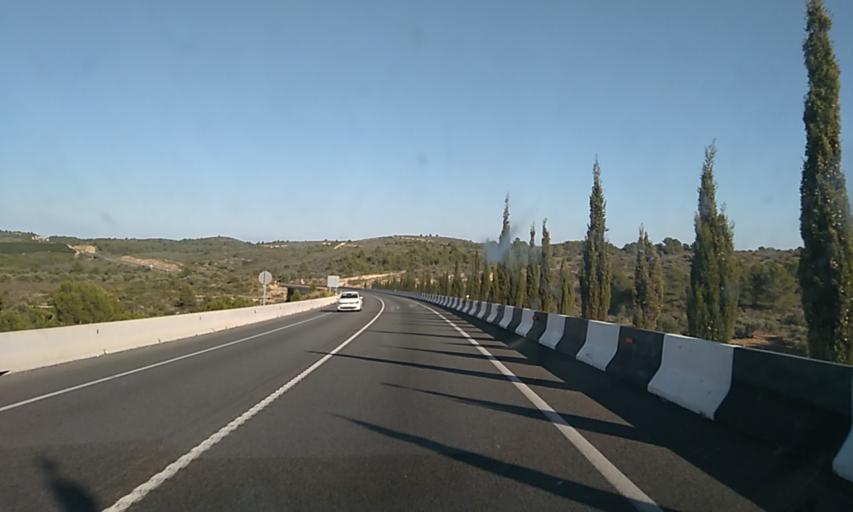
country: ES
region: Valencia
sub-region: Provincia de Castello
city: Torreblanca
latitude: 40.2101
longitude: 0.1364
